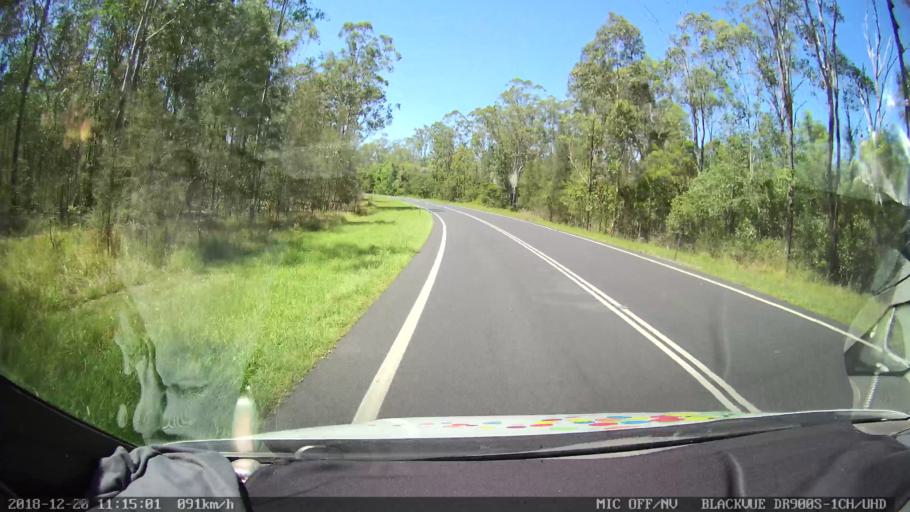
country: AU
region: New South Wales
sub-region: Richmond Valley
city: Casino
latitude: -29.0078
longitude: 153.0065
